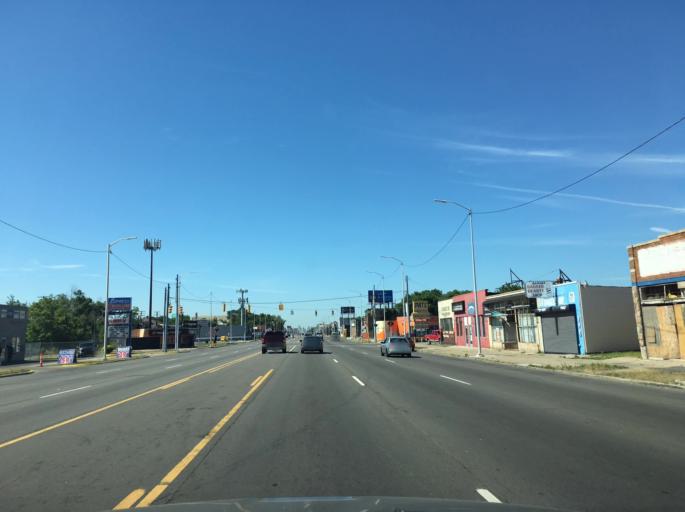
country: US
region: Michigan
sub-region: Macomb County
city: Eastpointe
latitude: 42.4322
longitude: -82.9796
